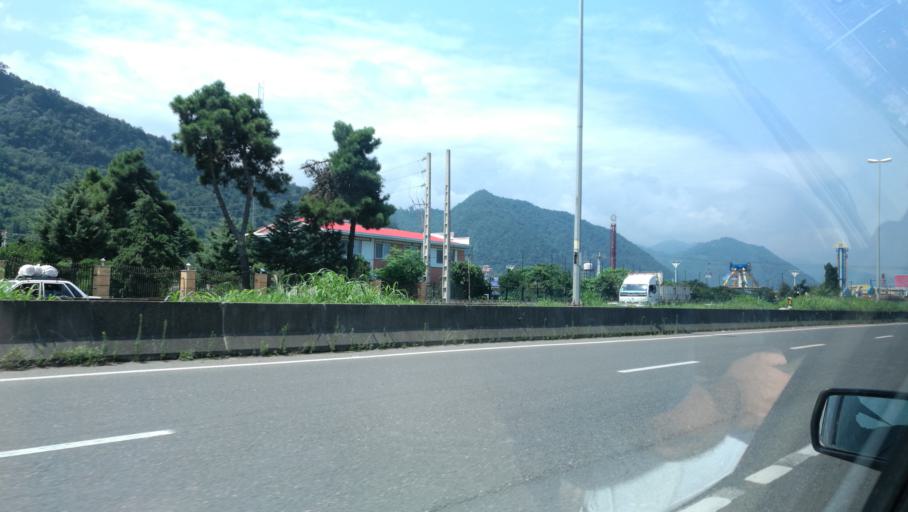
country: IR
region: Mazandaran
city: Ramsar
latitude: 36.9591
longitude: 50.6028
